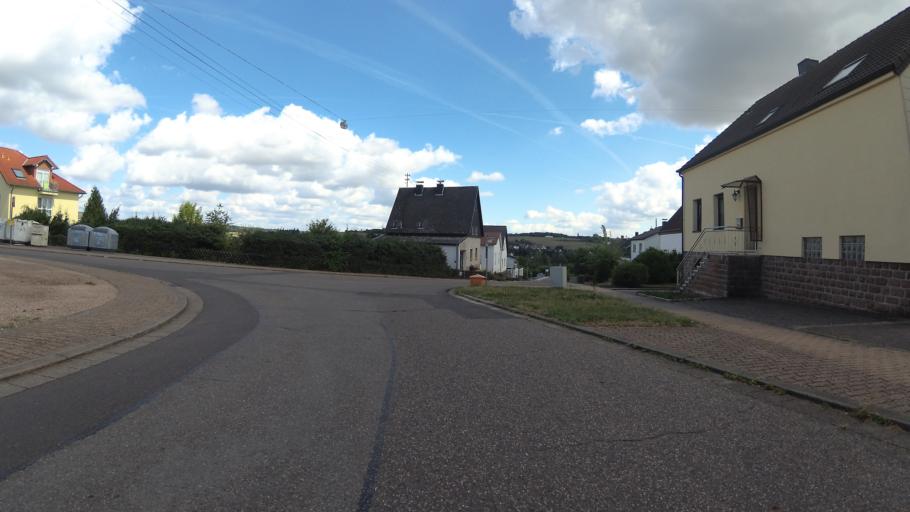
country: DE
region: Saarland
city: Illingen
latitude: 49.3704
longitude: 7.0474
